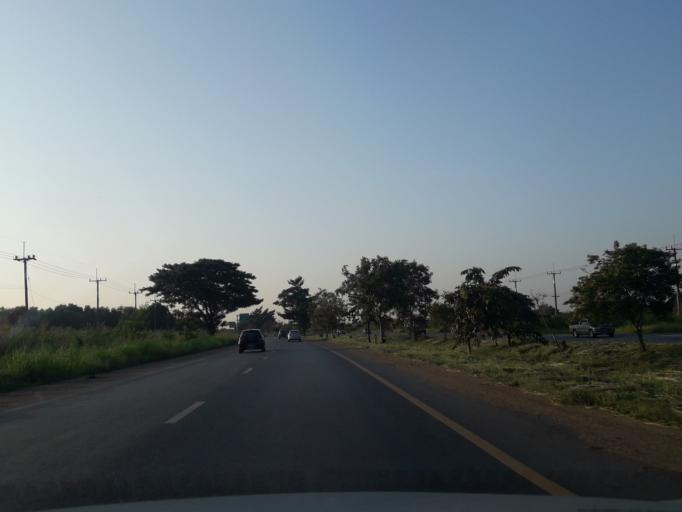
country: TH
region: Phra Nakhon Si Ayutthaya
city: Bang Pa-in
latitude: 14.2240
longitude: 100.5410
